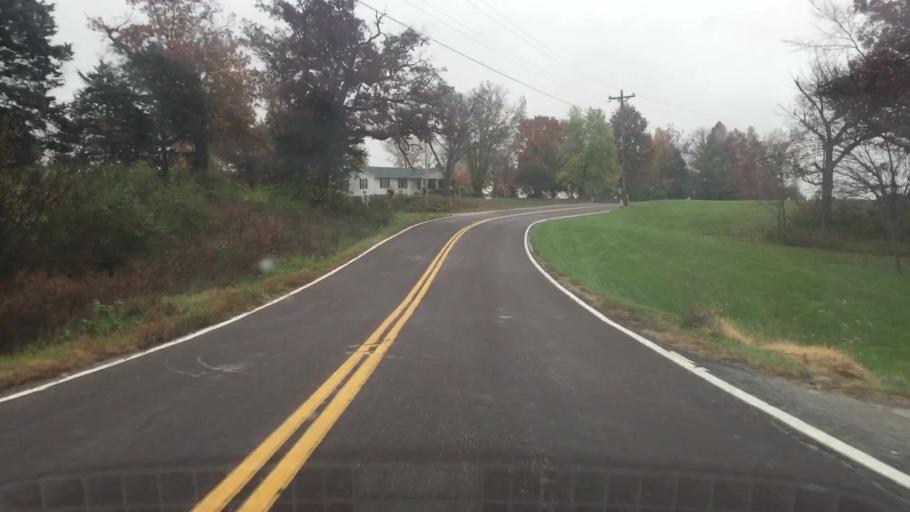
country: US
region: Missouri
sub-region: Callaway County
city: Fulton
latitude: 38.8188
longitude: -91.9071
